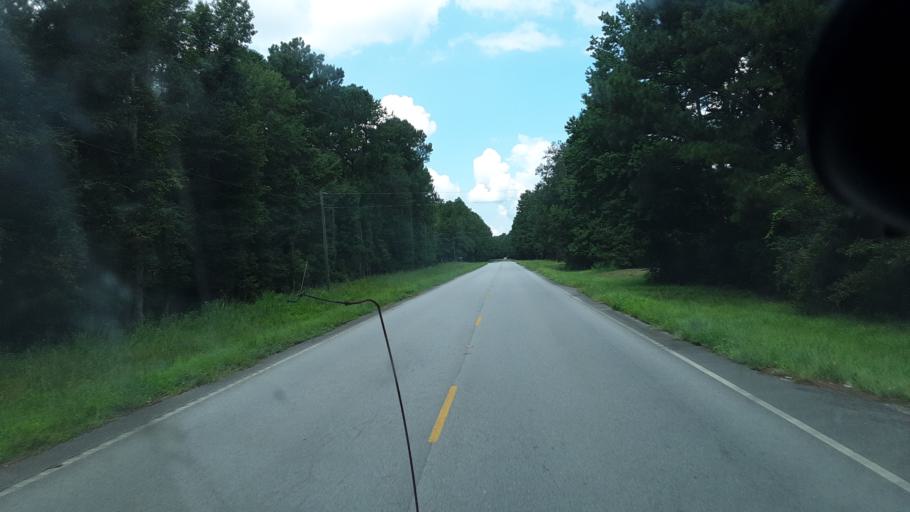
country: US
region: South Carolina
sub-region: Berkeley County
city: Saint Stephen
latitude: 33.2889
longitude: -79.7666
